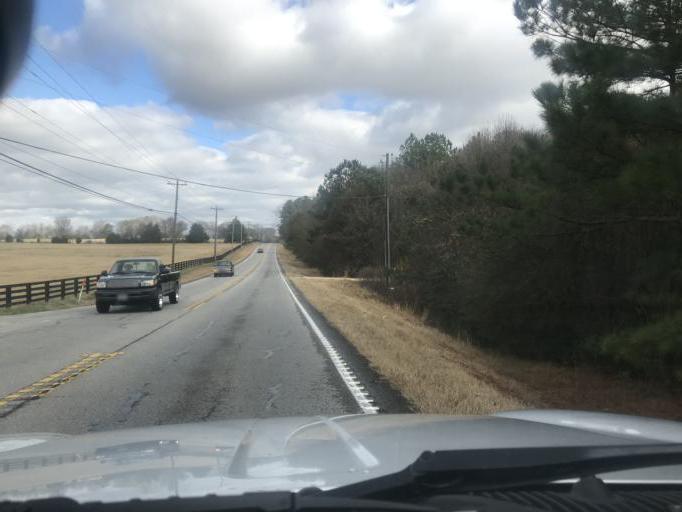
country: US
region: Georgia
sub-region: Barrow County
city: Russell
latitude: 34.0268
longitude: -83.6732
